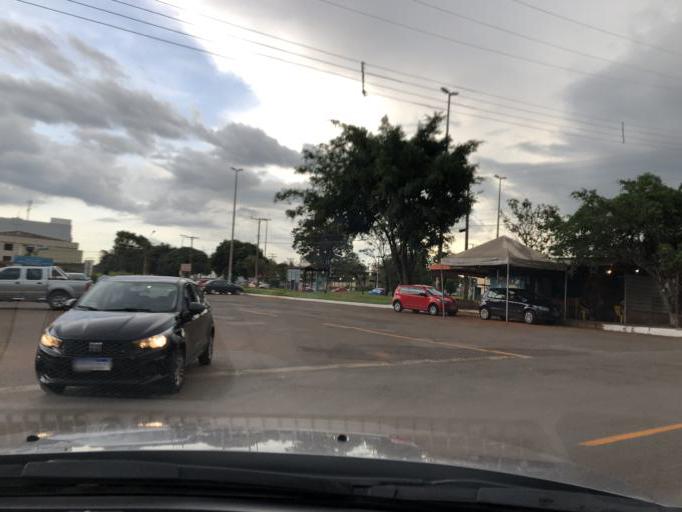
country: BR
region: Federal District
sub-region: Brasilia
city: Brasilia
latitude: -15.8263
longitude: -48.1132
